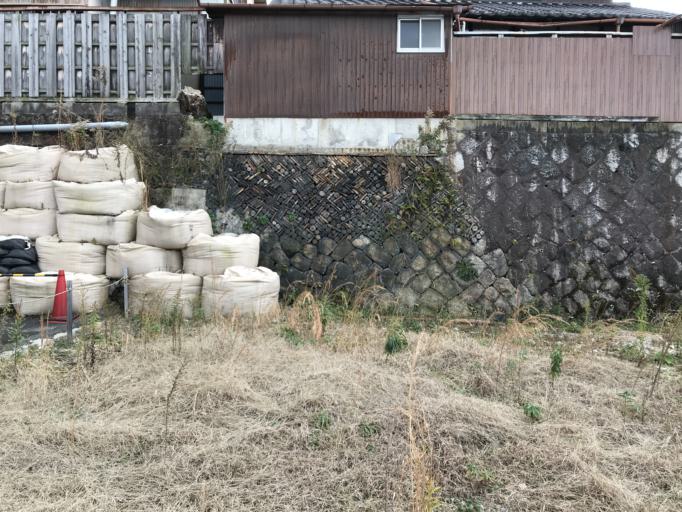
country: JP
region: Aichi
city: Seto
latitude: 35.2245
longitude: 137.1068
